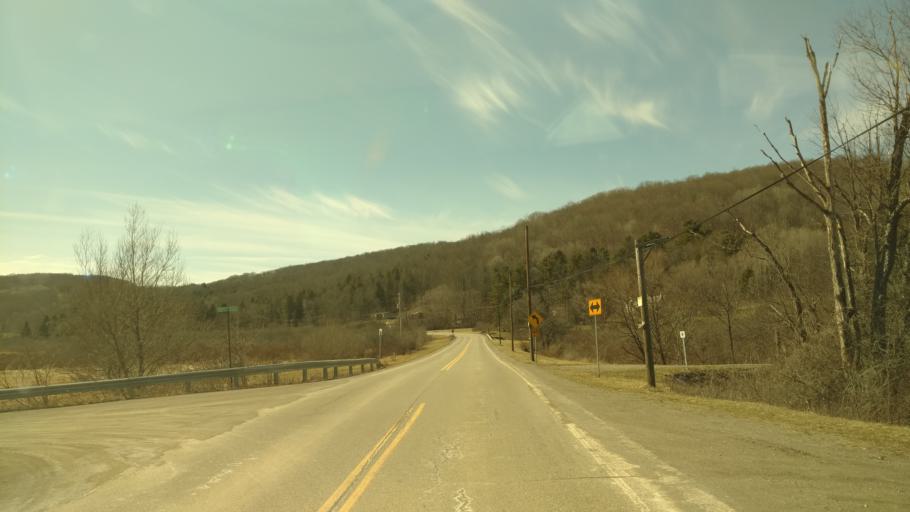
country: US
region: New York
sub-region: Allegany County
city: Wellsville
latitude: 42.0485
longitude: -77.9290
